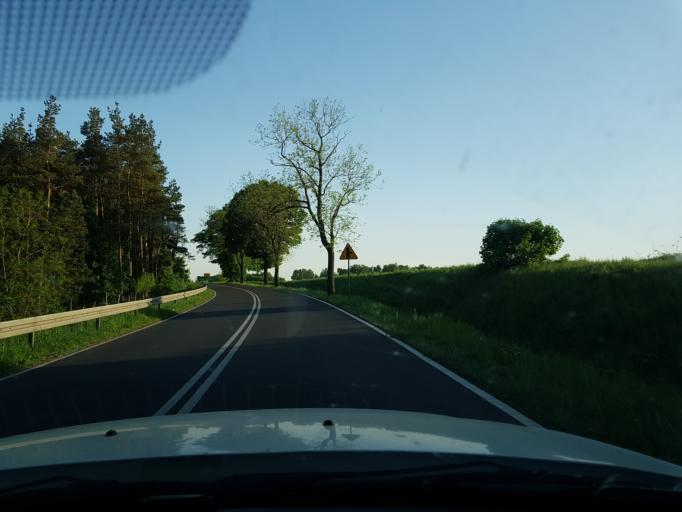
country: PL
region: West Pomeranian Voivodeship
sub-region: Powiat goleniowski
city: Maszewo
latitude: 53.4798
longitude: 15.0591
